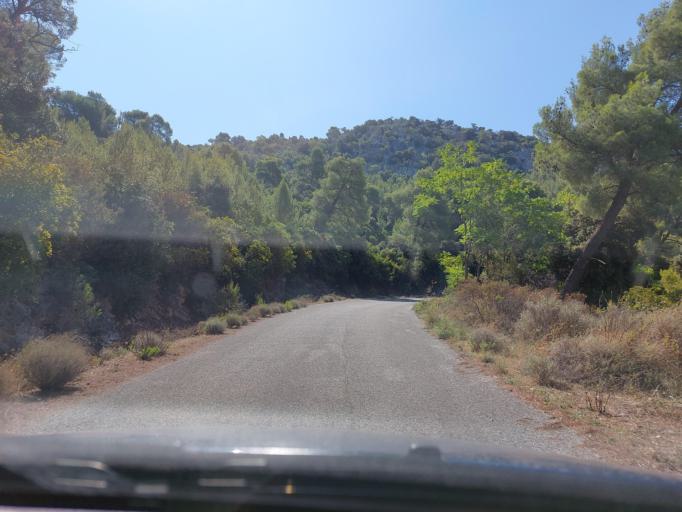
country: HR
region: Dubrovacko-Neretvanska
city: Smokvica
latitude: 42.7449
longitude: 16.8464
